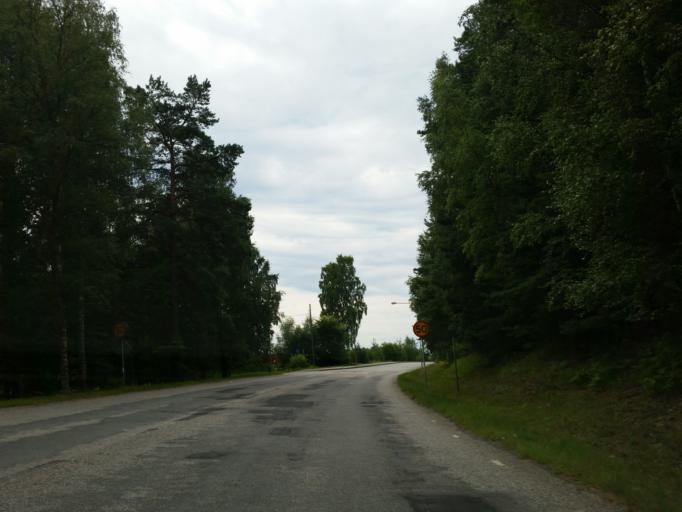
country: SE
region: Stockholm
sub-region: Sodertalje Kommun
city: Soedertaelje
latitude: 59.2091
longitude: 17.6515
